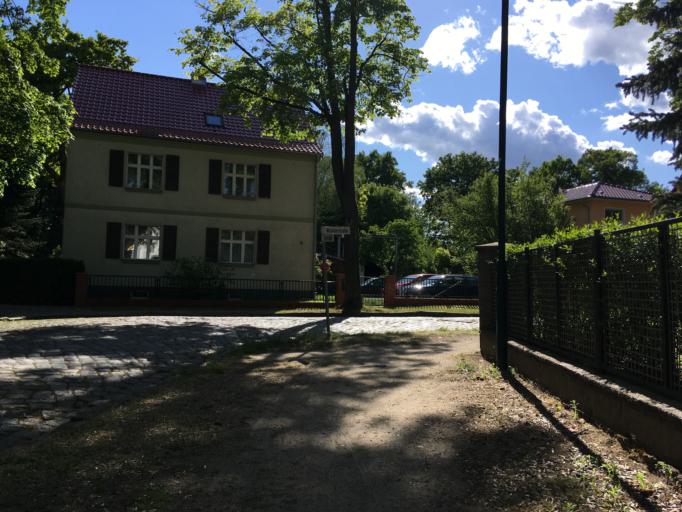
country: DE
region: Berlin
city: Buch
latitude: 52.6463
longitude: 13.5132
